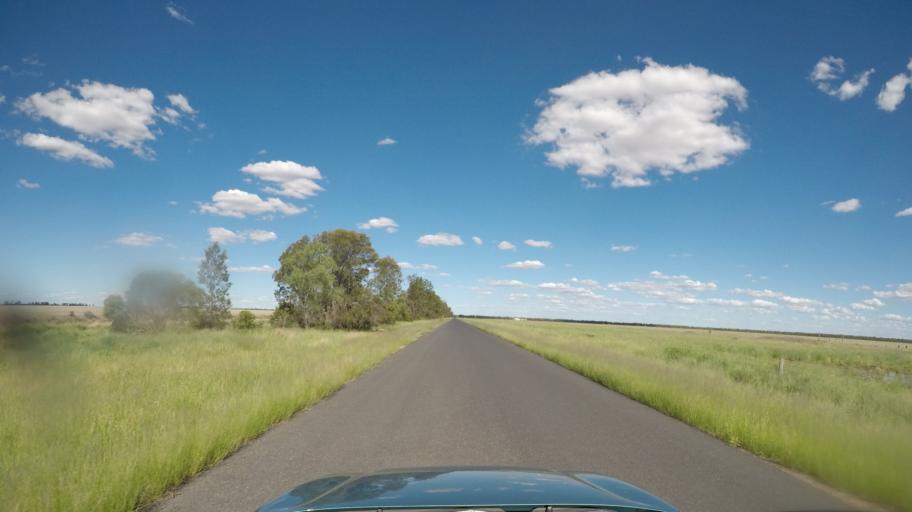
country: AU
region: Queensland
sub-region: Goondiwindi
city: Goondiwindi
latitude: -28.1766
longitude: 150.2617
